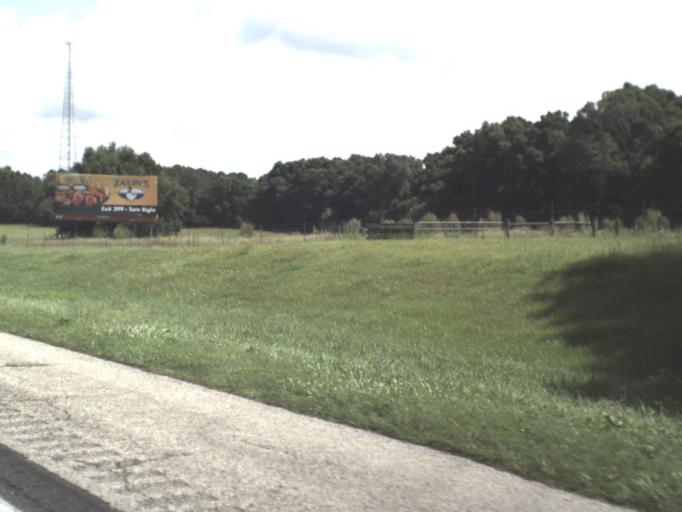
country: US
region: Florida
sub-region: Alachua County
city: Alachua
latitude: 29.7703
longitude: -82.5069
